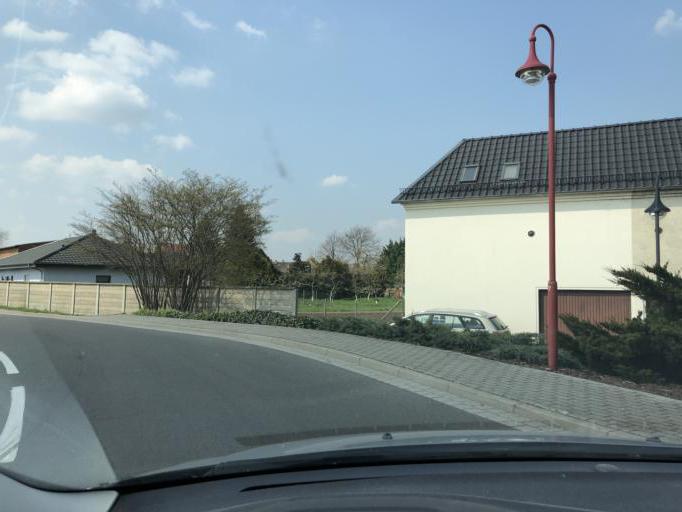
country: DE
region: Saxony
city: Wiedemar
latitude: 51.4702
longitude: 12.2321
